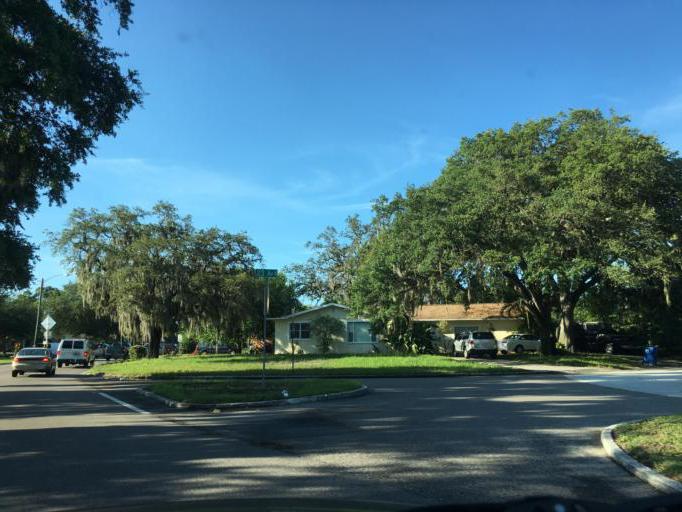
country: US
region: Florida
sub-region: Pinellas County
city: West and East Lealman
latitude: 27.7930
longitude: -82.7005
